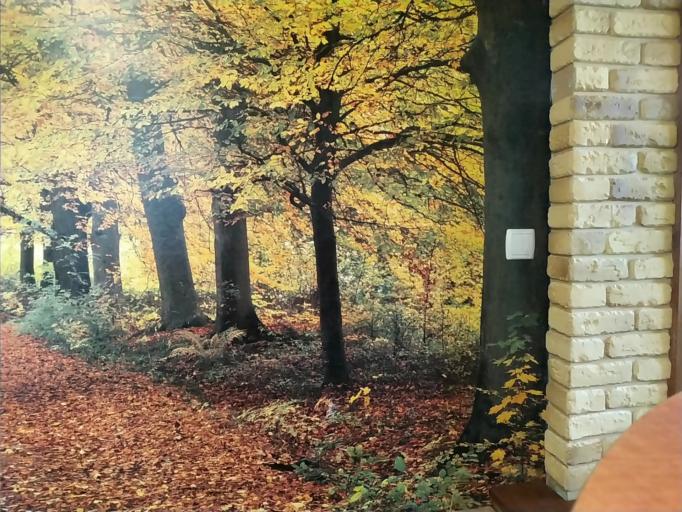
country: RU
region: Arkhangelskaya
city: Kargopol'
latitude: 60.9131
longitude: 38.8824
